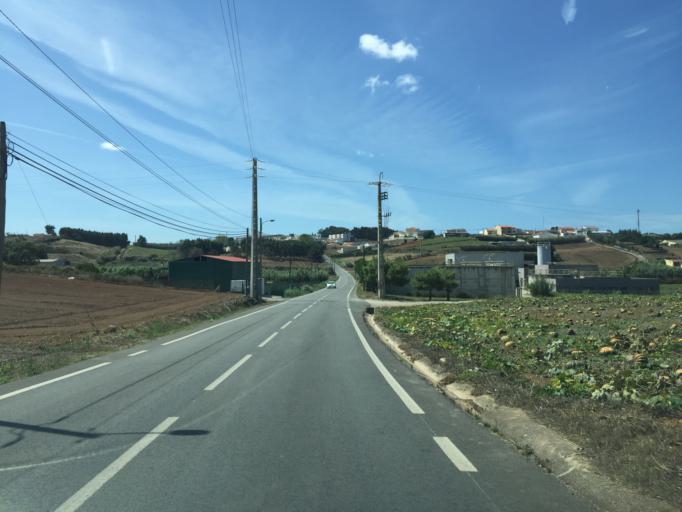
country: PT
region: Lisbon
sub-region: Lourinha
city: Lourinha
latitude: 39.2630
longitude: -9.3132
